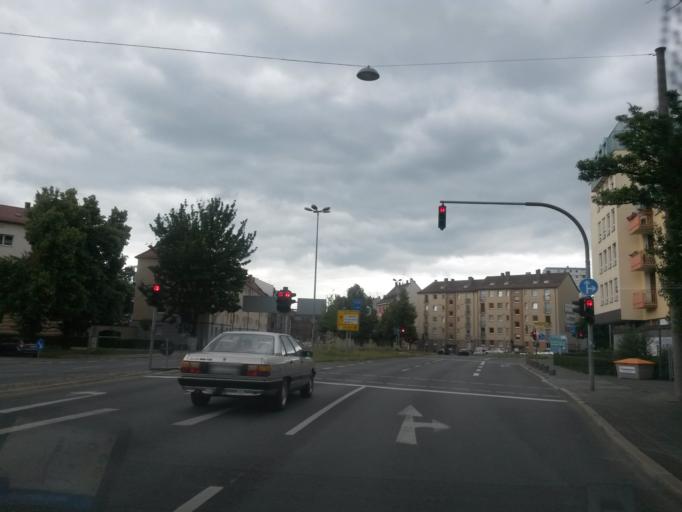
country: DE
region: Bavaria
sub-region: Regierungsbezirk Mittelfranken
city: Furth
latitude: 49.4808
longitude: 10.9995
